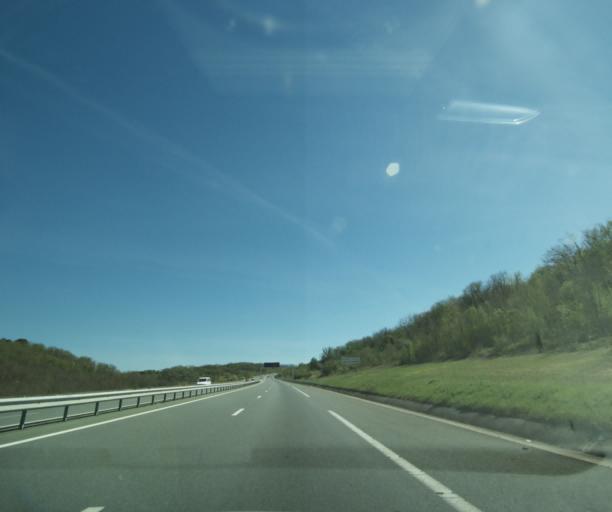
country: FR
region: Midi-Pyrenees
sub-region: Departement du Lot
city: Le Vigan
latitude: 44.7245
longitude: 1.5597
